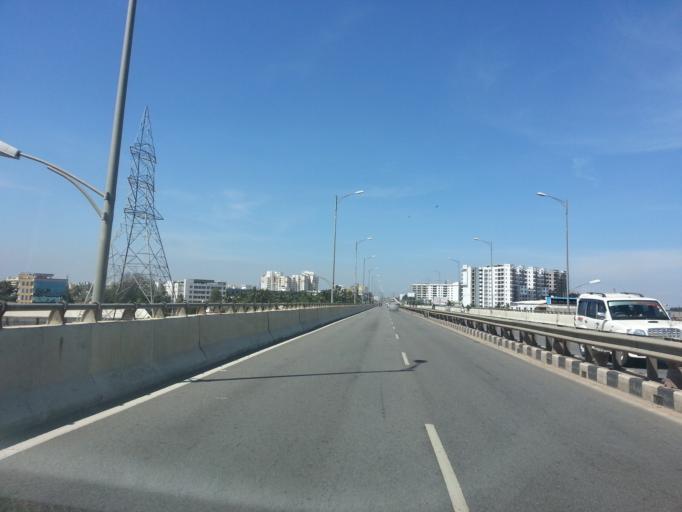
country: IN
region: Karnataka
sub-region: Bangalore Urban
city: Bangalore
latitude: 12.8584
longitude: 77.6624
